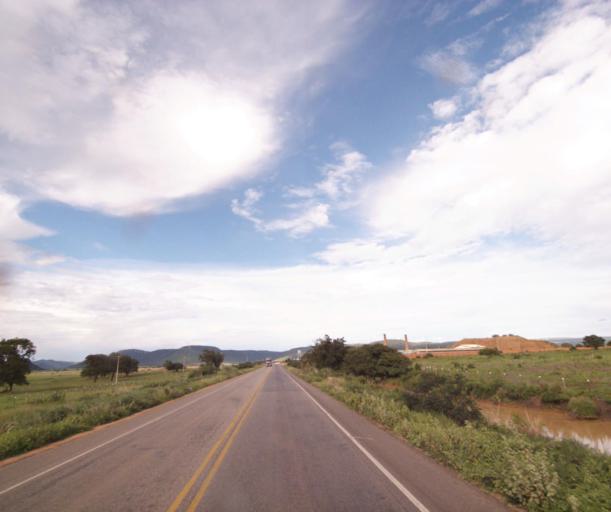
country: BR
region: Bahia
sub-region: Guanambi
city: Guanambi
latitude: -14.1929
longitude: -42.7461
